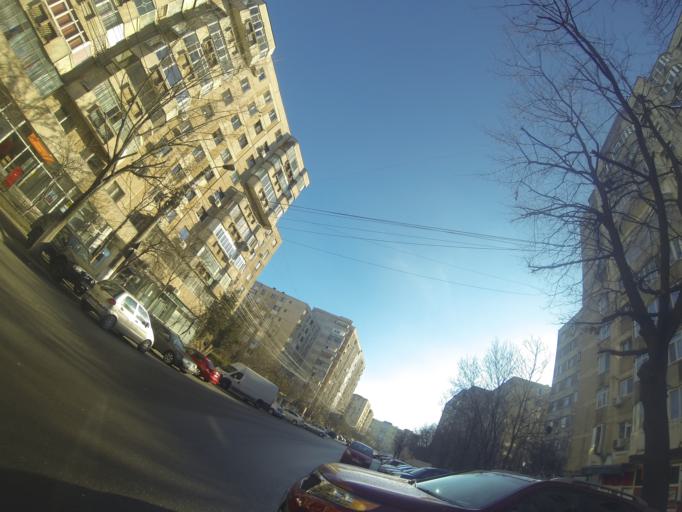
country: RO
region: Bucuresti
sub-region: Municipiul Bucuresti
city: Bucuresti
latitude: 44.4105
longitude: 26.0641
